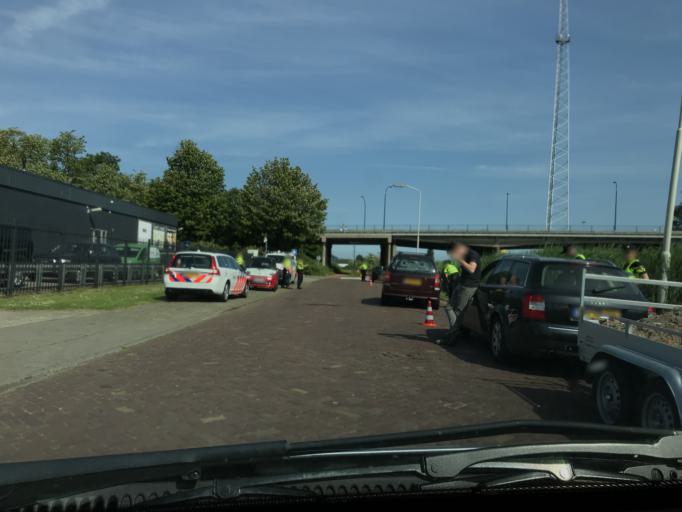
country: NL
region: North Brabant
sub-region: Gemeente Breda
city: Breda
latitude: 51.6007
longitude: 4.7629
